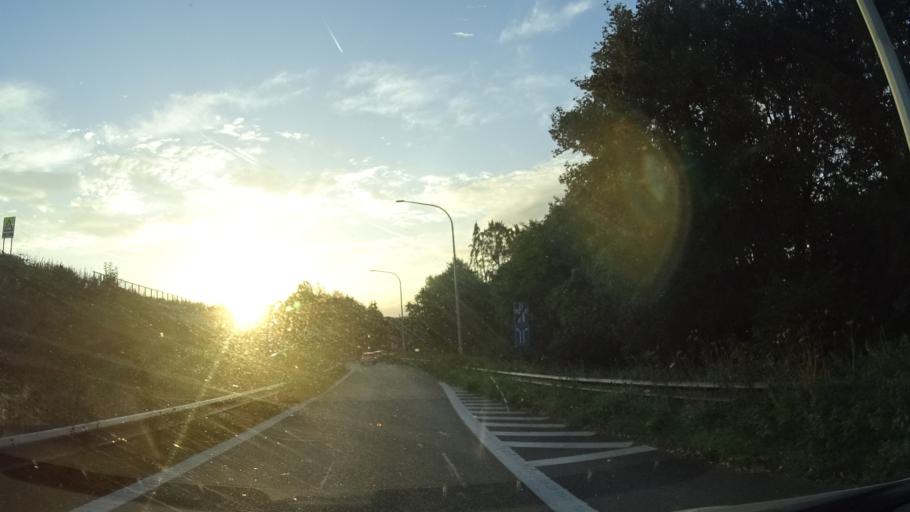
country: BE
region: Wallonia
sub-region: Province du Hainaut
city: Chasse Royale
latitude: 50.4054
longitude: 3.9600
